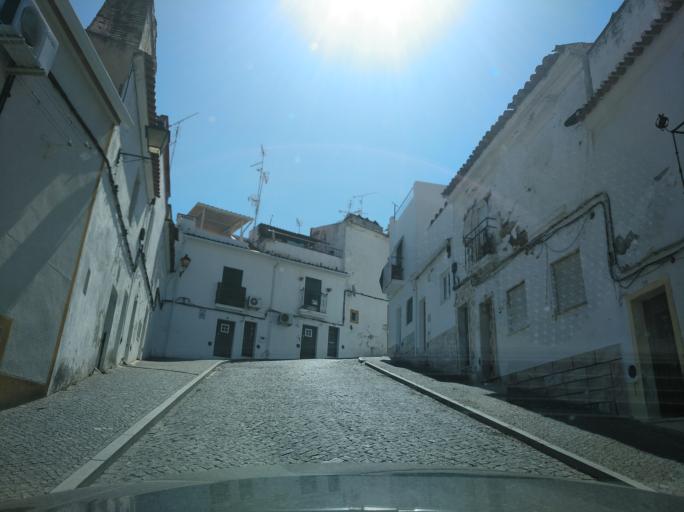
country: PT
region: Portalegre
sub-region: Campo Maior
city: Campo Maior
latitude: 39.0122
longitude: -7.0718
